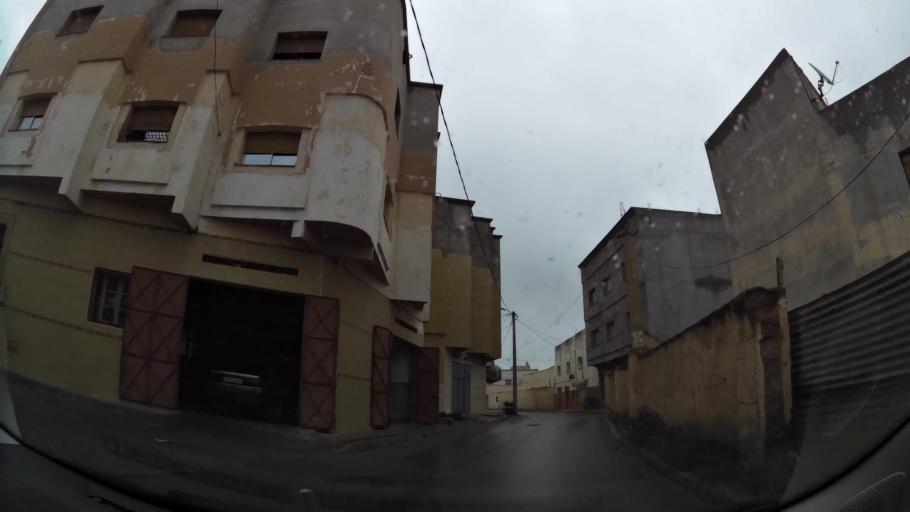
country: MA
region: Oriental
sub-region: Nador
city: Nador
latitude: 35.1639
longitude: -2.9539
